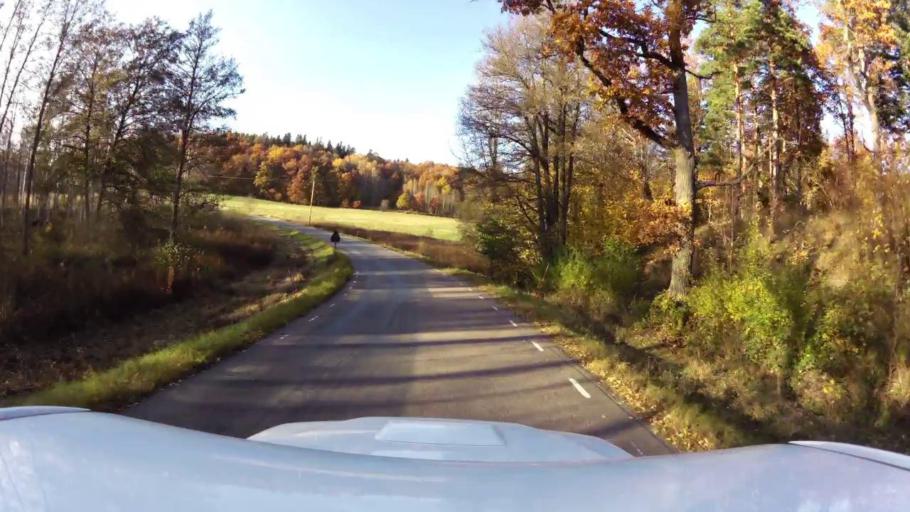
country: SE
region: OEstergoetland
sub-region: Kinda Kommun
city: Rimforsa
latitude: 58.1729
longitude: 15.6870
